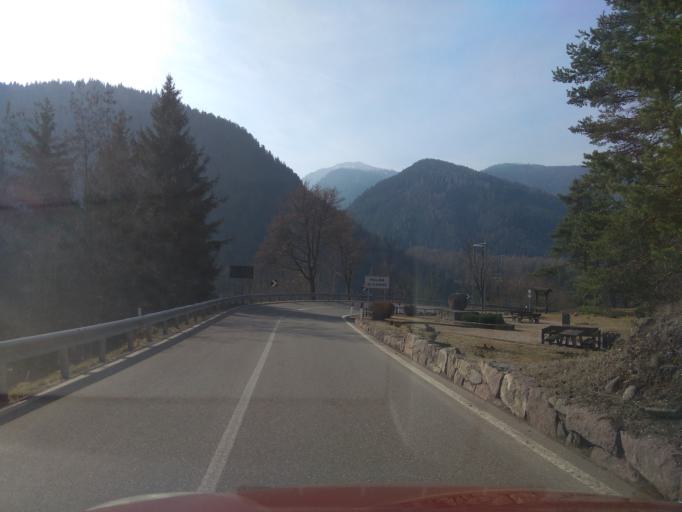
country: IT
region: Trentino-Alto Adige
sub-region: Provincia di Trento
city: Castello Molina di Fiemme
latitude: 46.2750
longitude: 11.4215
